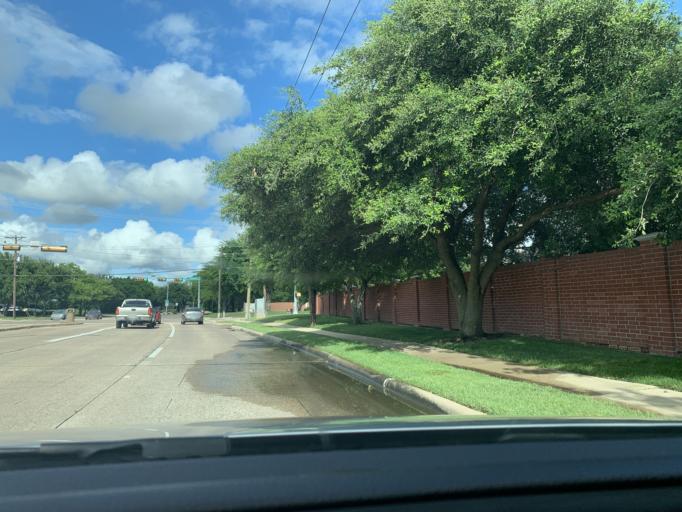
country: US
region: Texas
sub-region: Dallas County
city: Grand Prairie
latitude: 32.6582
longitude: -97.0160
